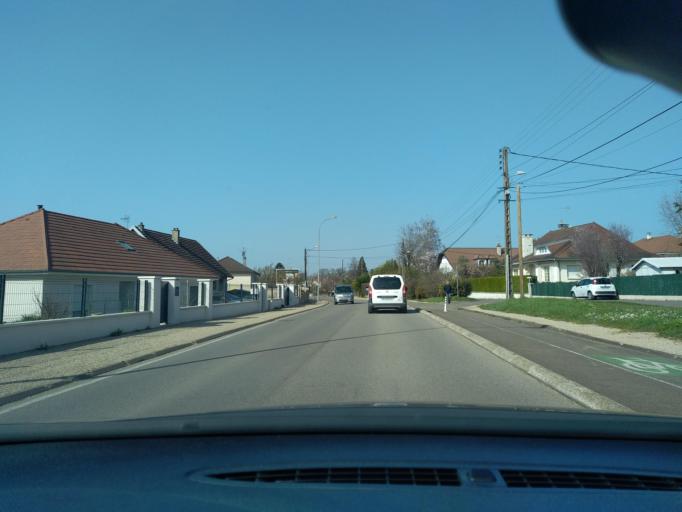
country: FR
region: Franche-Comte
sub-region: Departement du Jura
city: Dole
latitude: 47.0740
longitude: 5.5021
